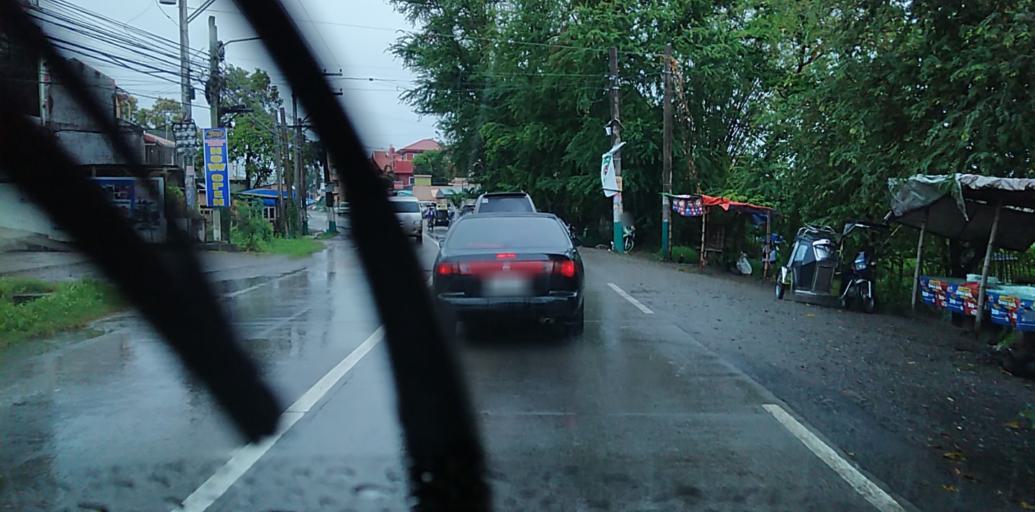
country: PH
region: Central Luzon
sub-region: Province of Pampanga
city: Mexico
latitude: 15.0584
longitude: 120.7183
